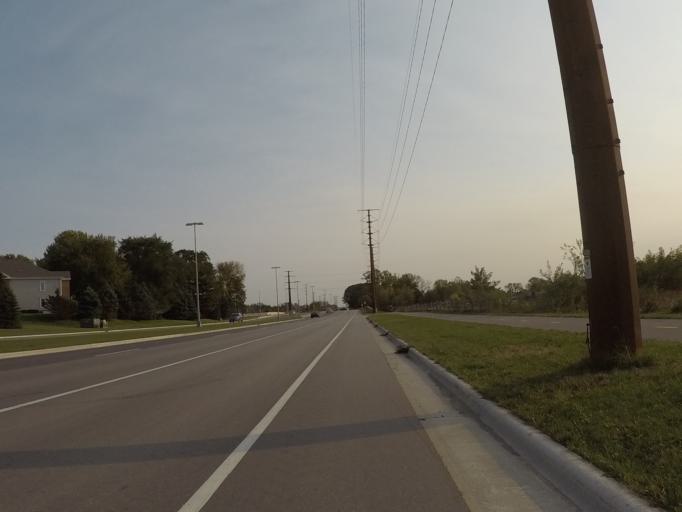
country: US
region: Wisconsin
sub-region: Dane County
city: Verona
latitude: 43.0272
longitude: -89.5335
